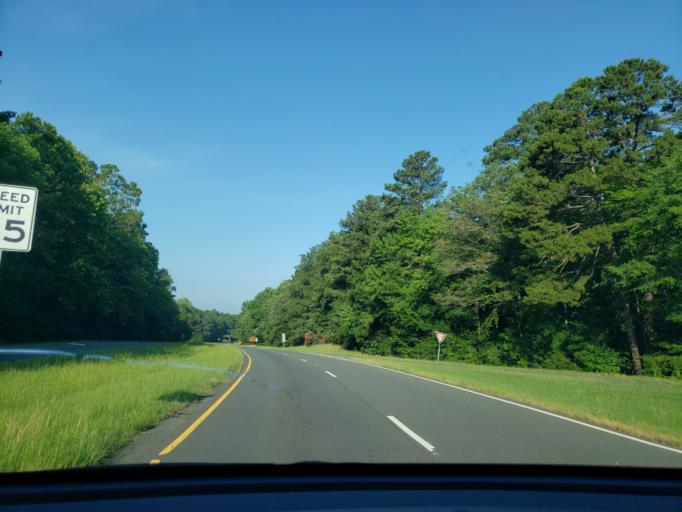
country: US
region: North Carolina
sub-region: Durham County
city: Durham
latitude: 35.9746
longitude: -78.9379
